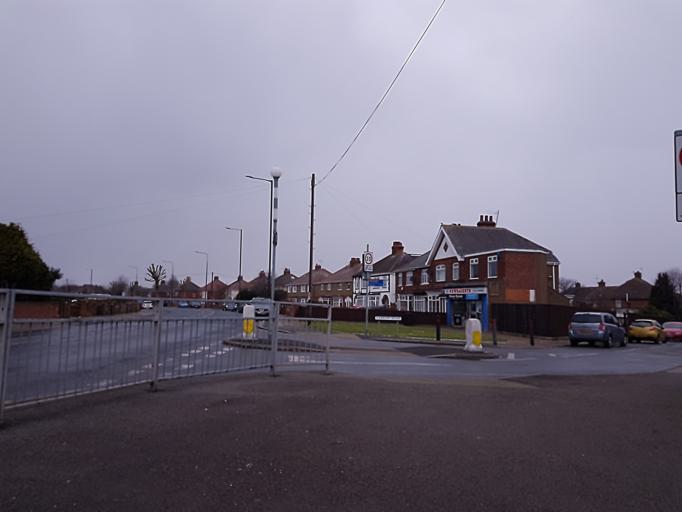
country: GB
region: England
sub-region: North East Lincolnshire
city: Grimbsy
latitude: 53.5626
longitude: -0.1156
